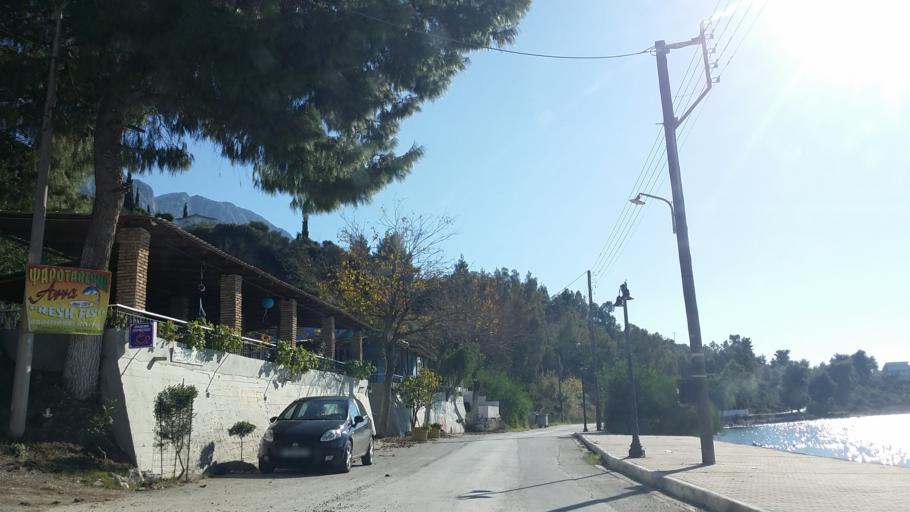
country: GR
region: West Greece
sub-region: Nomos Aitolias kai Akarnanias
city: Palairos
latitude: 38.7784
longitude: 20.8809
